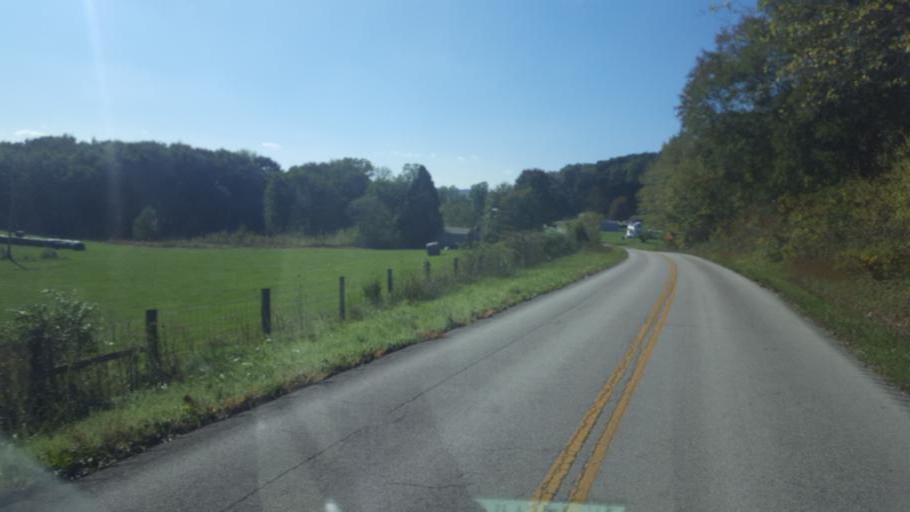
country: US
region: Kentucky
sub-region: Fleming County
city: Flemingsburg
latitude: 38.4686
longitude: -83.5569
